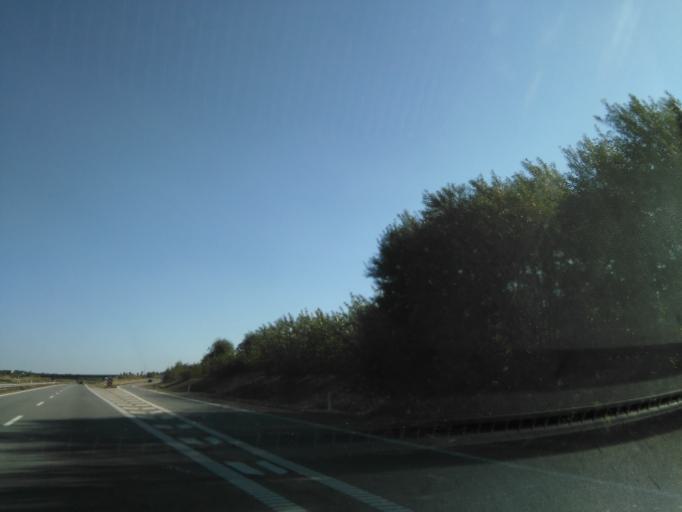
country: DK
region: Central Jutland
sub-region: Arhus Kommune
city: Hjortshoj
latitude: 56.2302
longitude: 10.2597
